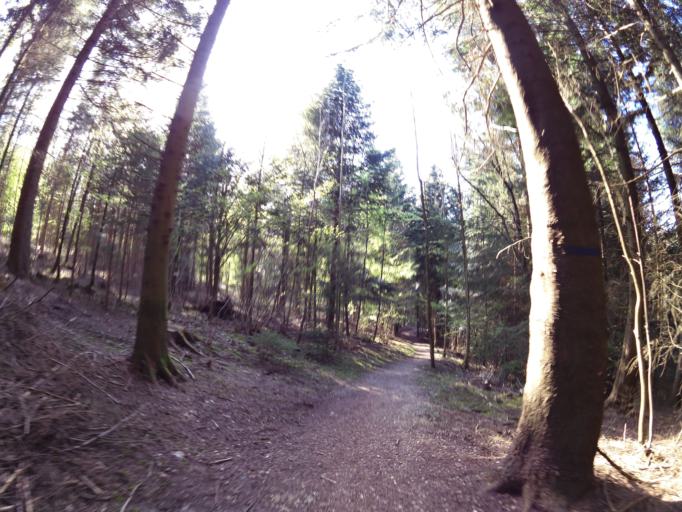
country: CH
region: Aargau
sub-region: Bezirk Aarau
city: Aarau
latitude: 47.4010
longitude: 8.0351
